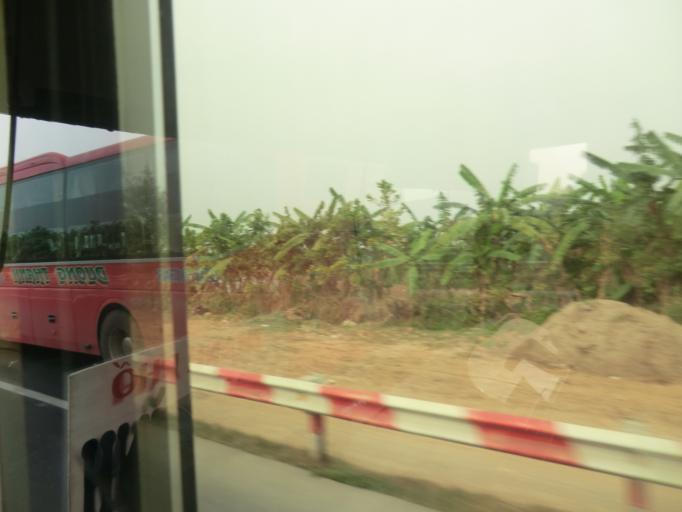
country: VN
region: Ha Noi
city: Thuong Tin
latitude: 20.8775
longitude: 105.8750
